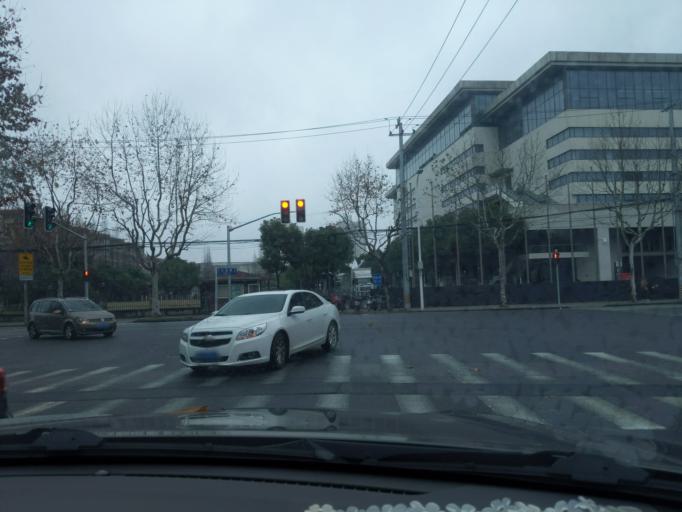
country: CN
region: Shanghai Shi
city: Luwan
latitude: 31.1843
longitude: 121.5006
